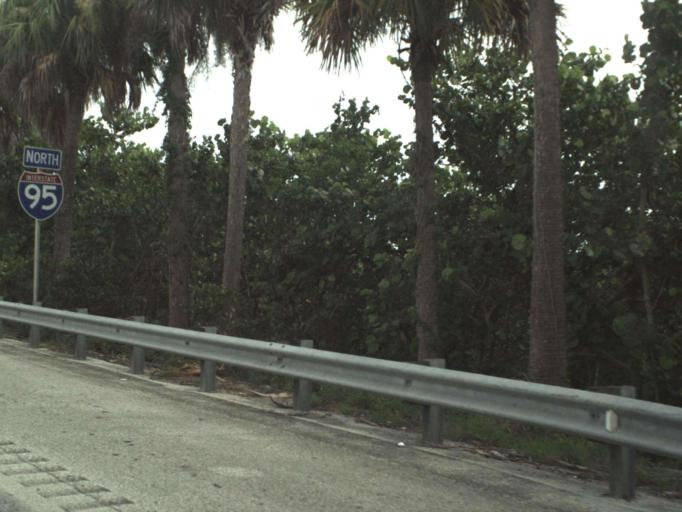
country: US
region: Florida
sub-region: Martin County
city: Palm City
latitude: 27.1170
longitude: -80.2663
